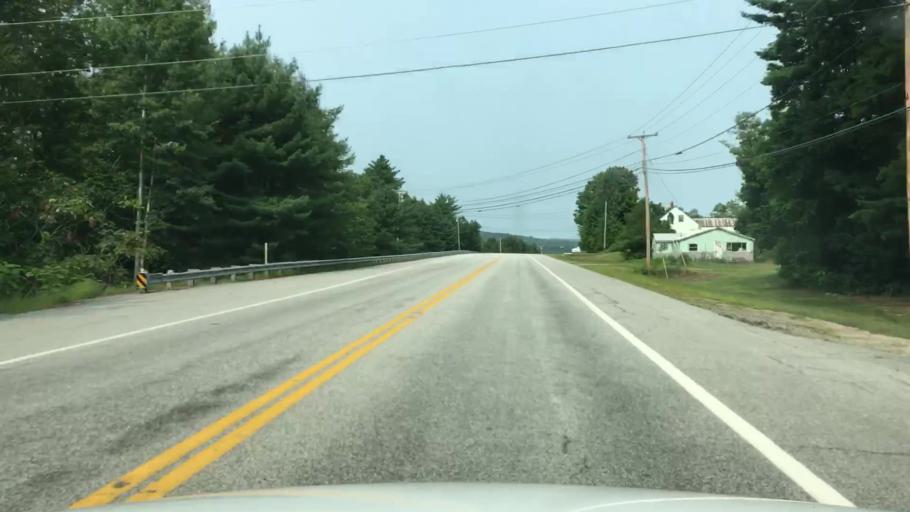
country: US
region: Maine
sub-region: Androscoggin County
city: Livermore Falls
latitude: 44.4493
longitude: -70.1635
